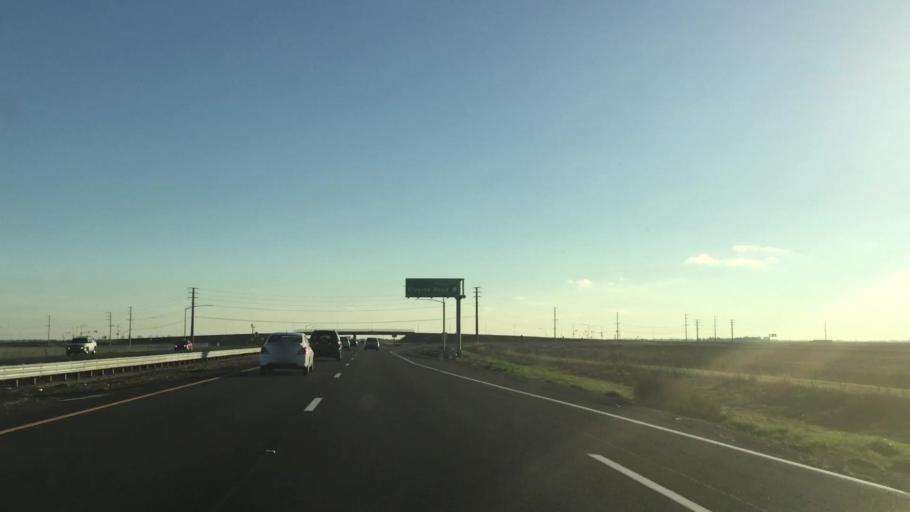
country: US
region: California
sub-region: Sacramento County
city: Elverta
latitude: 38.7209
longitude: -121.5405
